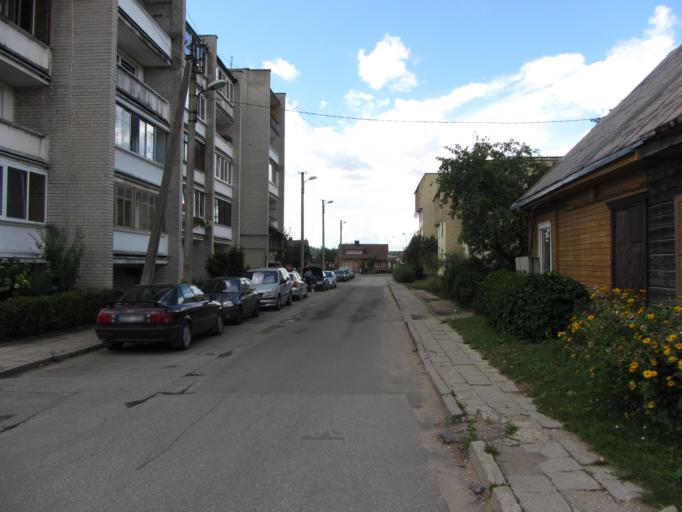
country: LT
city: Nemencine
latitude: 54.8486
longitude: 25.4699
